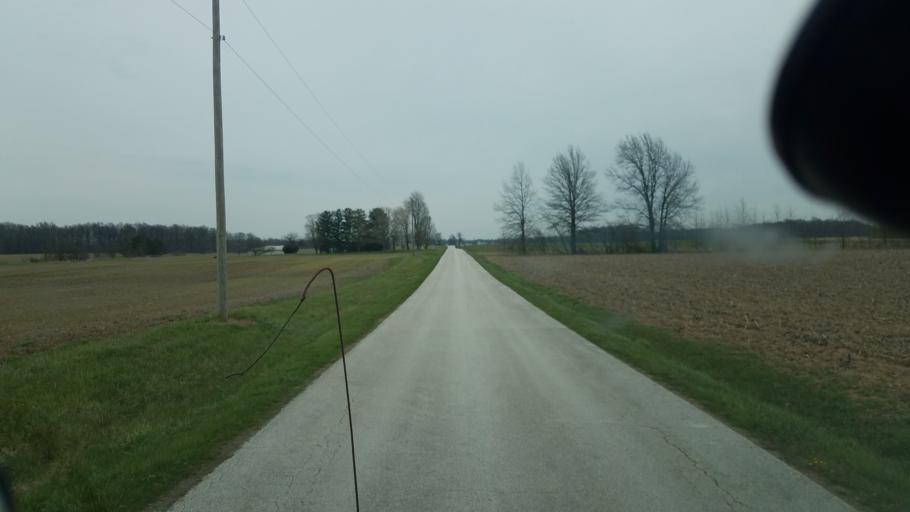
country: US
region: Ohio
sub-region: Hardin County
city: Forest
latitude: 40.7889
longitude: -83.4670
